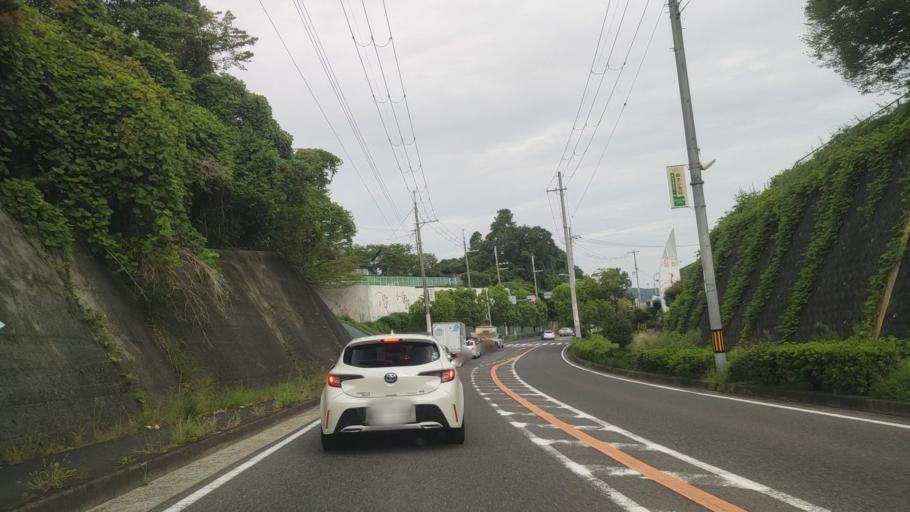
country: JP
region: Osaka
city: Tondabayashicho
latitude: 34.4350
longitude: 135.5585
